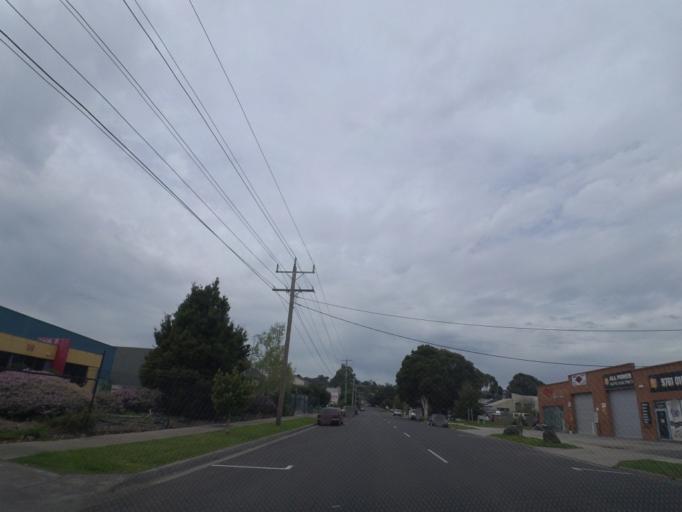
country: AU
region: Victoria
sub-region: Knox
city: Bayswater
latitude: -37.8478
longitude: 145.2821
